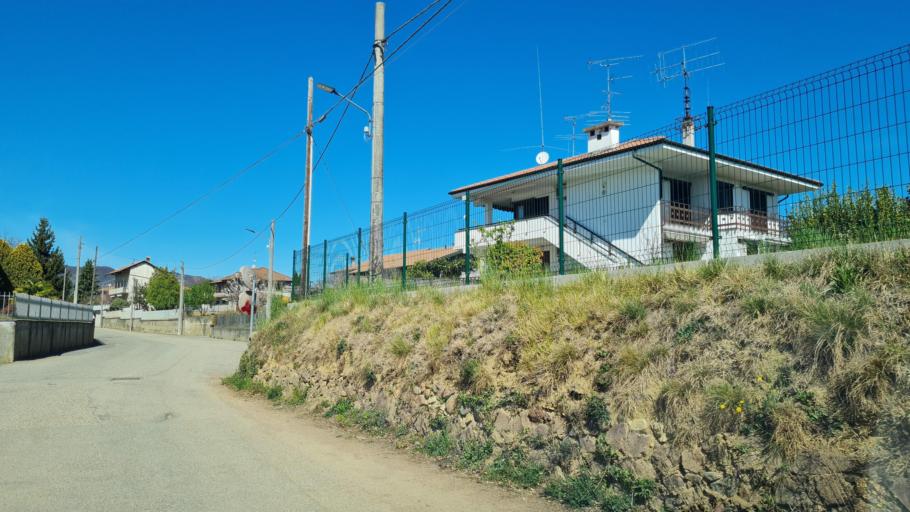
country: IT
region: Piedmont
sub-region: Provincia di Novara
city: Maggiora
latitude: 45.6868
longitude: 8.4334
